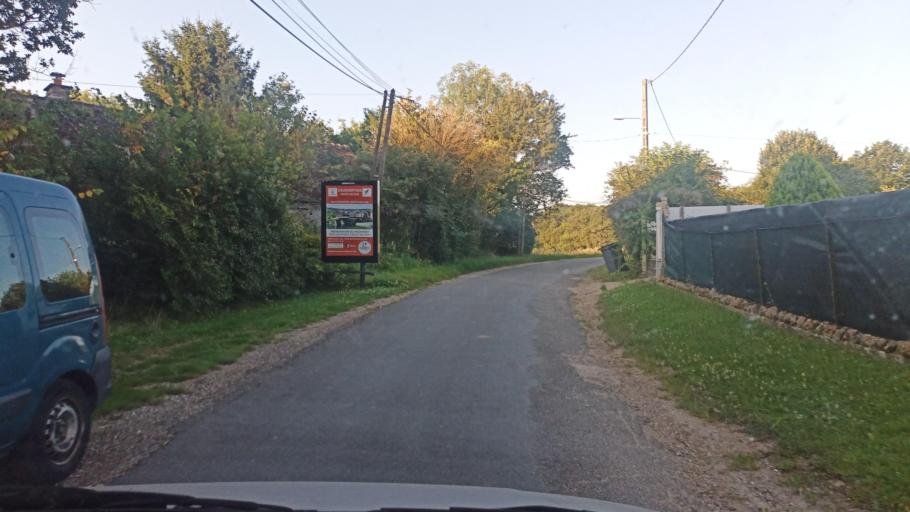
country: FR
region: Bourgogne
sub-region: Departement de l'Yonne
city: Pont-sur-Yonne
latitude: 48.2588
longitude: 3.1789
